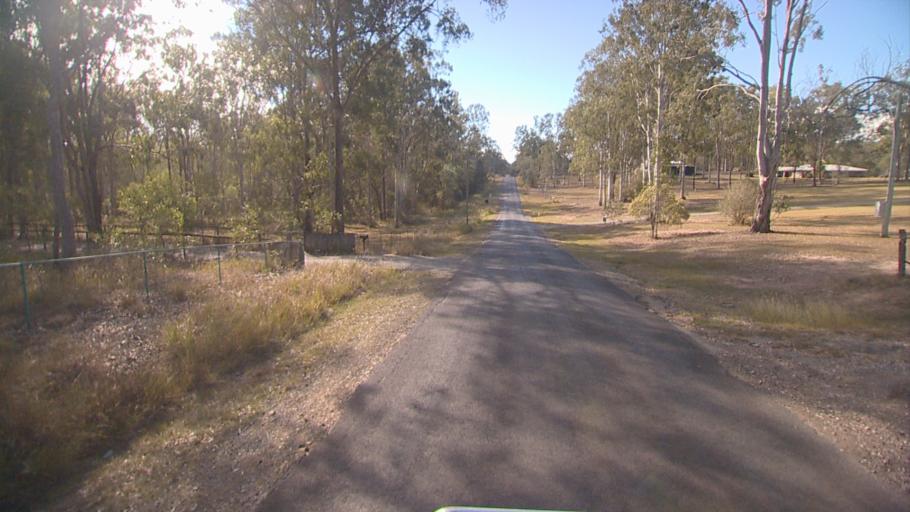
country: AU
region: Queensland
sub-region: Logan
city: Cedar Vale
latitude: -27.8298
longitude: 153.0618
